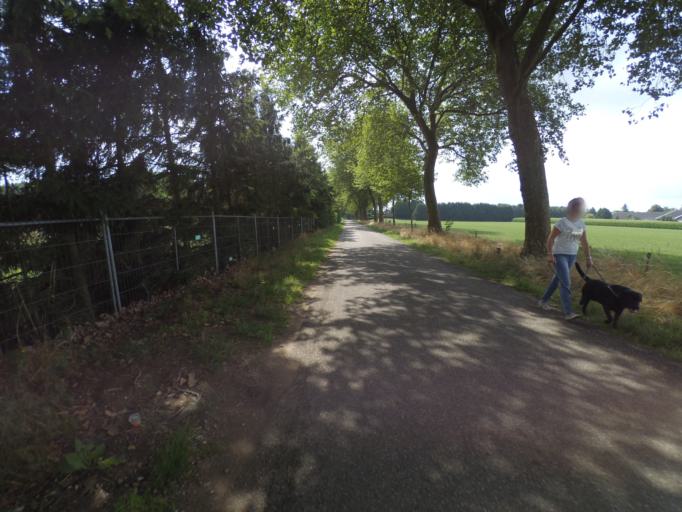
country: NL
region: Limburg
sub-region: Gemeente Echt-Susteren
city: Koningsbosch
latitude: 51.0607
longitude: 5.9399
